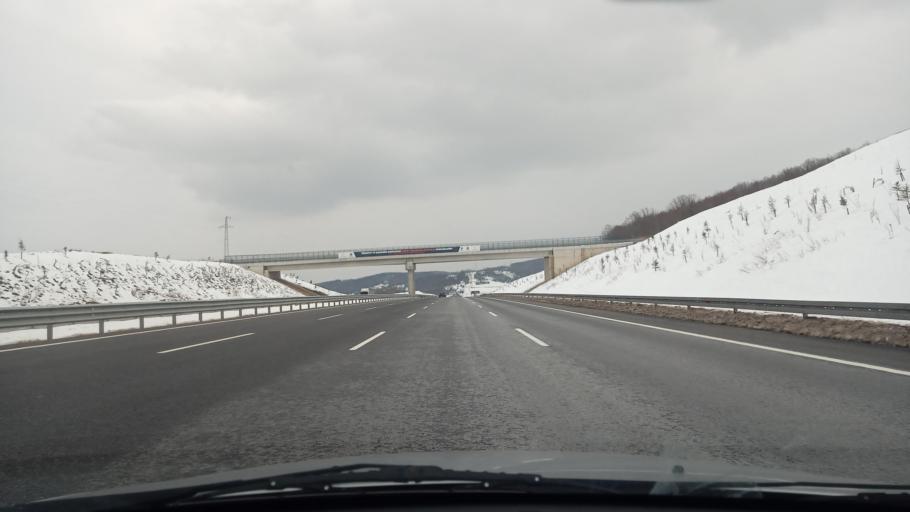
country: TR
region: Kocaeli
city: Izmit
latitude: 40.8609
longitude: 29.8599
